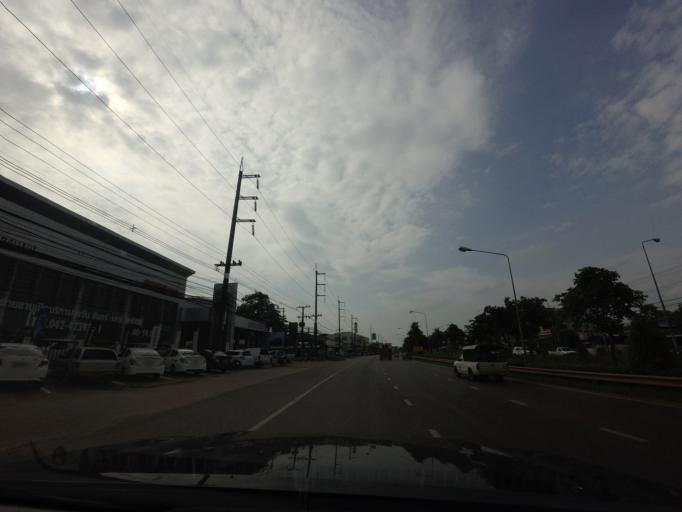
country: TH
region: Nong Khai
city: Nong Khai
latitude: 17.8627
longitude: 102.7490
